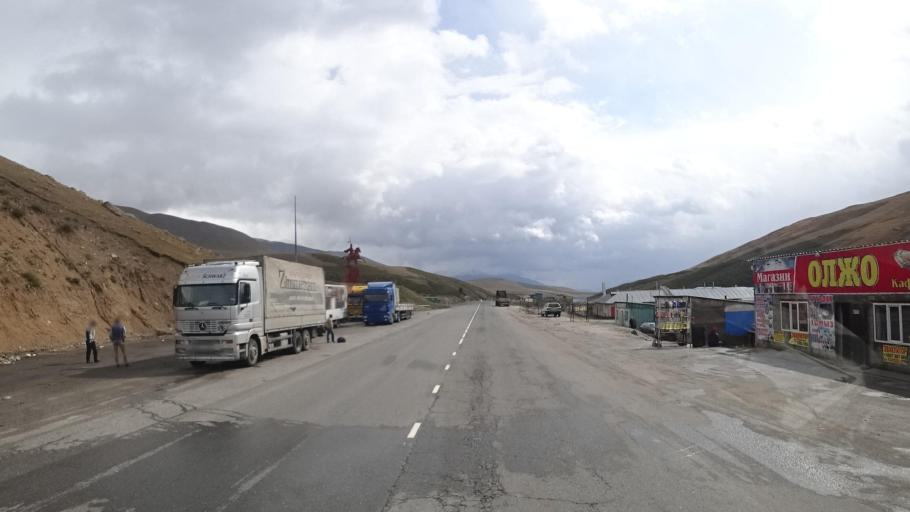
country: KG
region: Jalal-Abad
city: Uch-Terek
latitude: 42.2072
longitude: 73.2493
